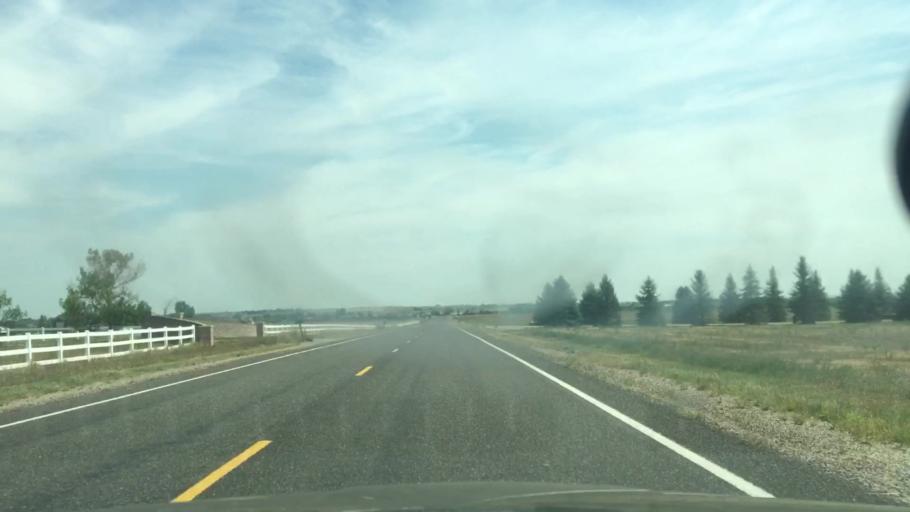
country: US
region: Colorado
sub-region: Larimer County
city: Berthoud
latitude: 40.3348
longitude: -105.1579
